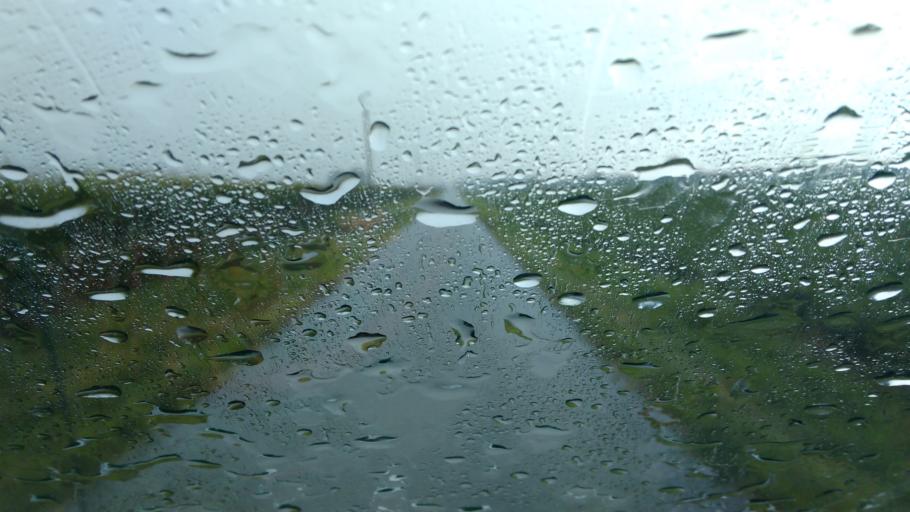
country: US
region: Ohio
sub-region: Hardin County
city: Kenton
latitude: 40.7167
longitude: -83.5582
